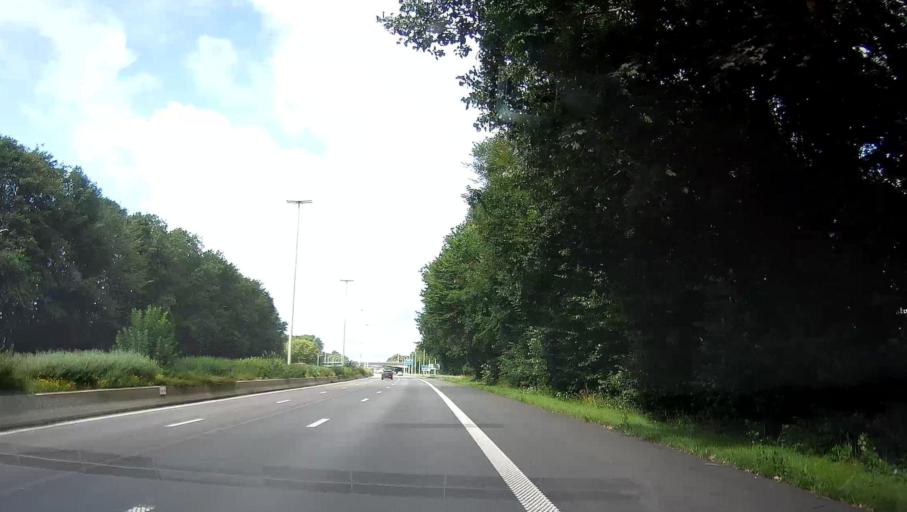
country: BE
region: Wallonia
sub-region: Province de Namur
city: Noville-les-Bois
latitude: 50.5329
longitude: 5.0156
